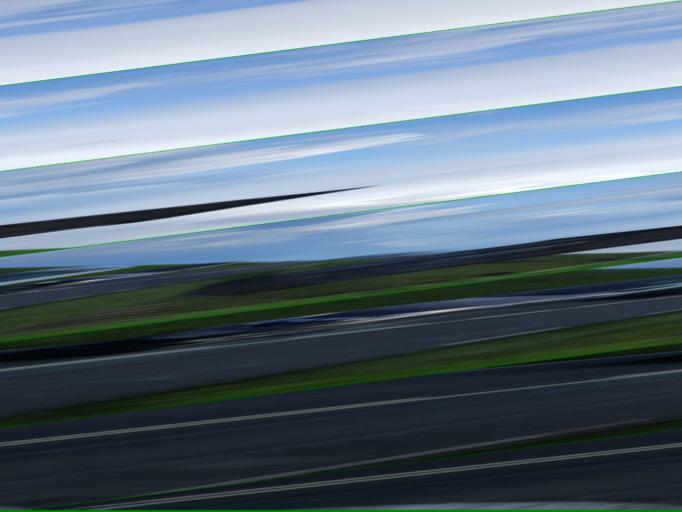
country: FR
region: Picardie
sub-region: Departement de l'Oise
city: Chaumont-en-Vexin
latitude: 49.2555
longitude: 1.8771
